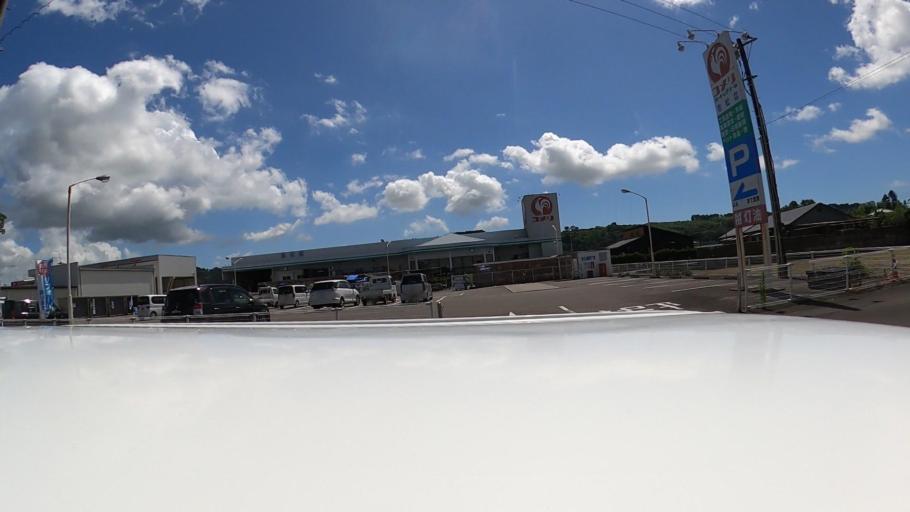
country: JP
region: Miyazaki
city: Tsuma
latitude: 32.0972
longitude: 131.4091
